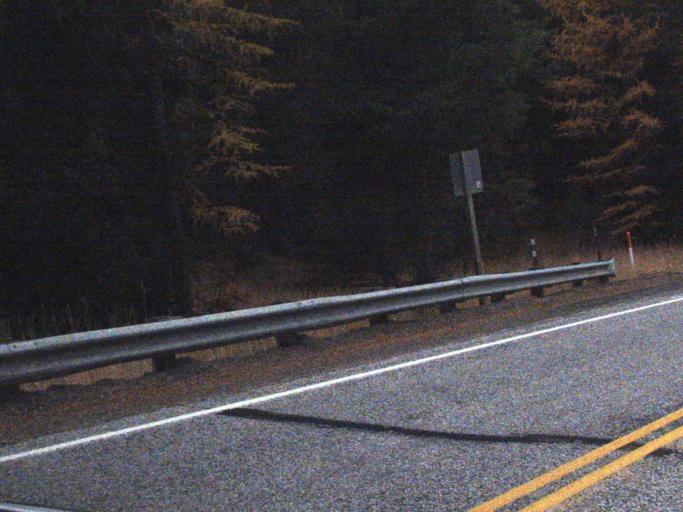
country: US
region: Washington
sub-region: Ferry County
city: Republic
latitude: 48.6125
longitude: -118.5749
